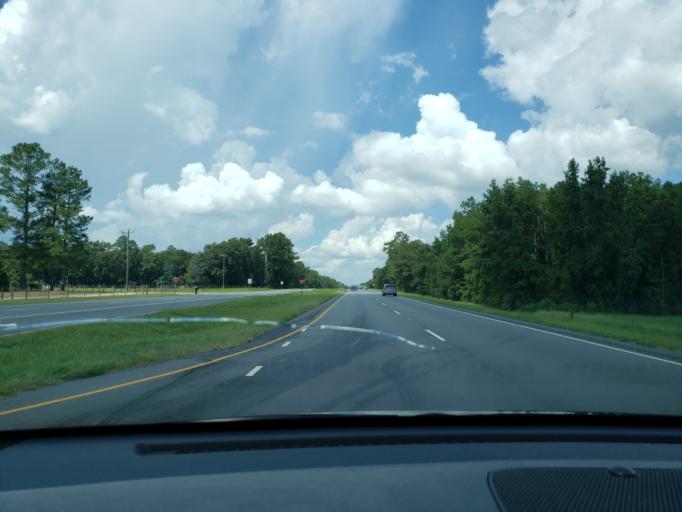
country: US
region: North Carolina
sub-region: Robeson County
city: Saint Pauls
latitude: 34.8062
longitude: -78.8292
